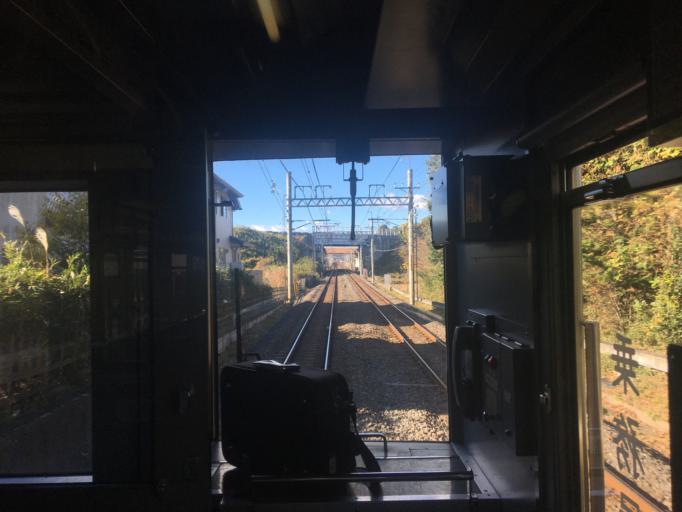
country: JP
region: Saitama
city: Ogawa
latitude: 36.0460
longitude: 139.3527
